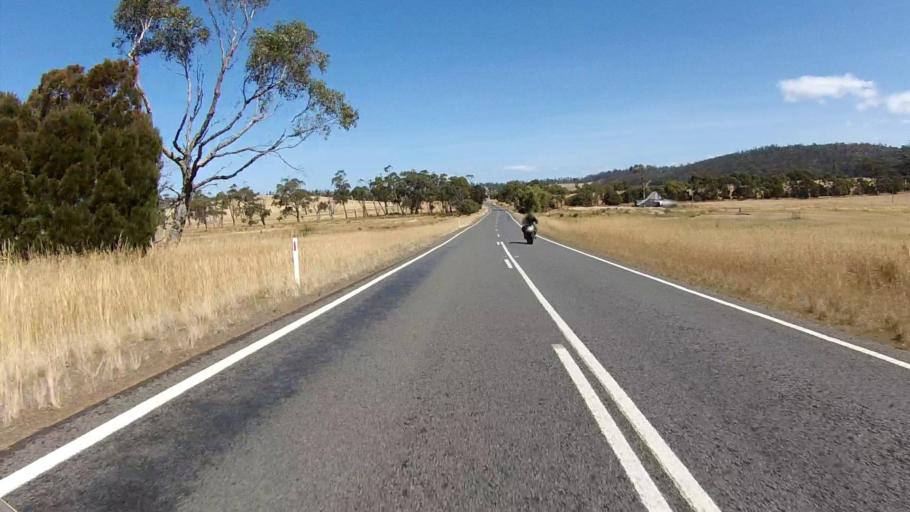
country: AU
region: Tasmania
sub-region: Sorell
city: Sorell
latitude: -42.4535
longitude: 147.9297
